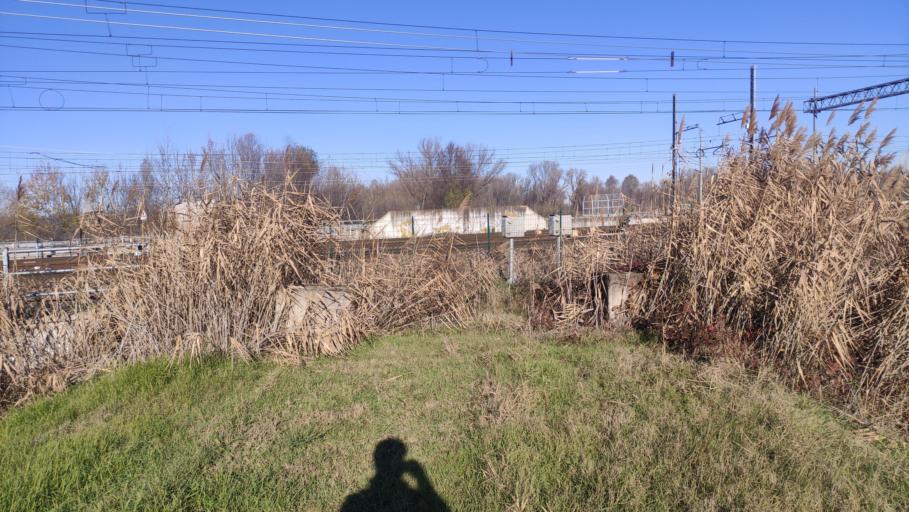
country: IT
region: Emilia-Romagna
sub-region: Provincia di Modena
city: Campogalliano
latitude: 44.6544
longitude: 10.8442
